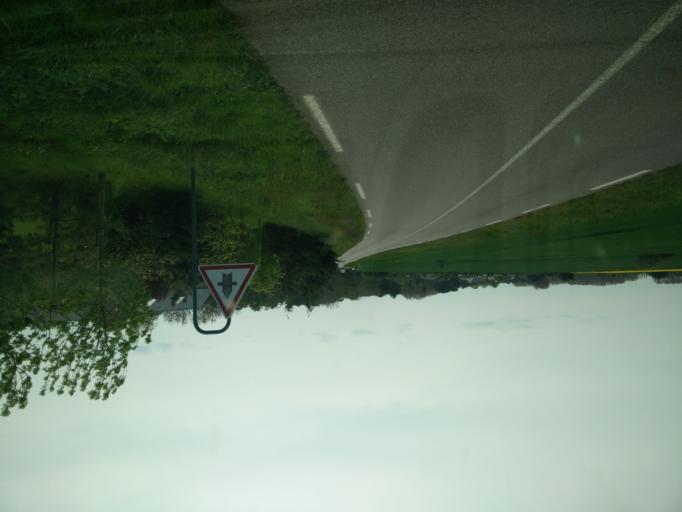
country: FR
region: Brittany
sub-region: Departement des Cotes-d'Armor
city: Plurien
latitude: 48.6572
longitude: -2.3484
